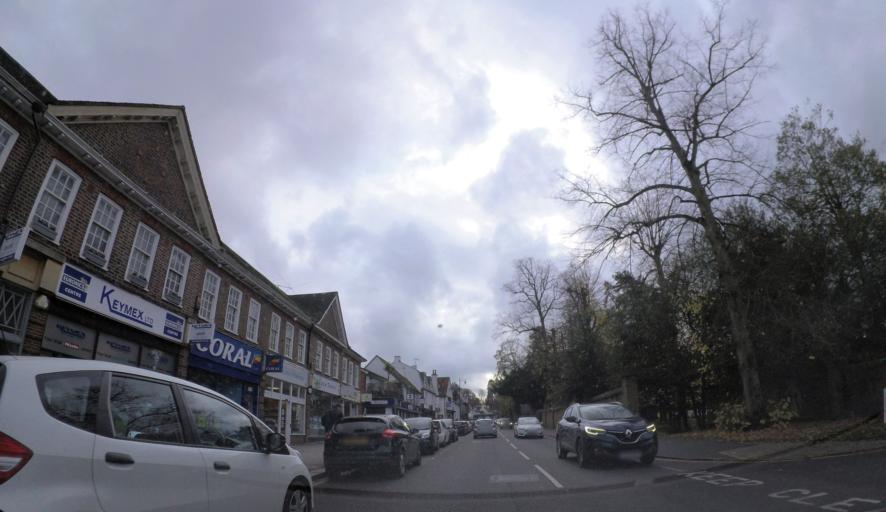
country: GB
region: England
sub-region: Surrey
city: Reigate
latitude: 51.2359
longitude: -0.2048
